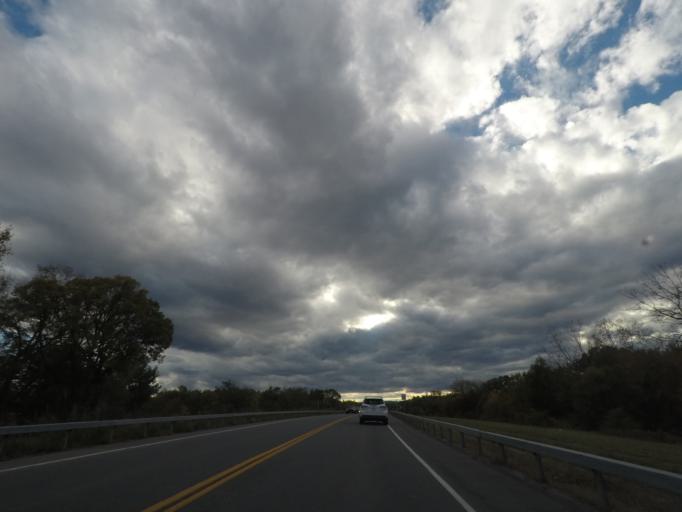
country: US
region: New York
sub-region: Albany County
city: Colonie
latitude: 42.7260
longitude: -73.8595
